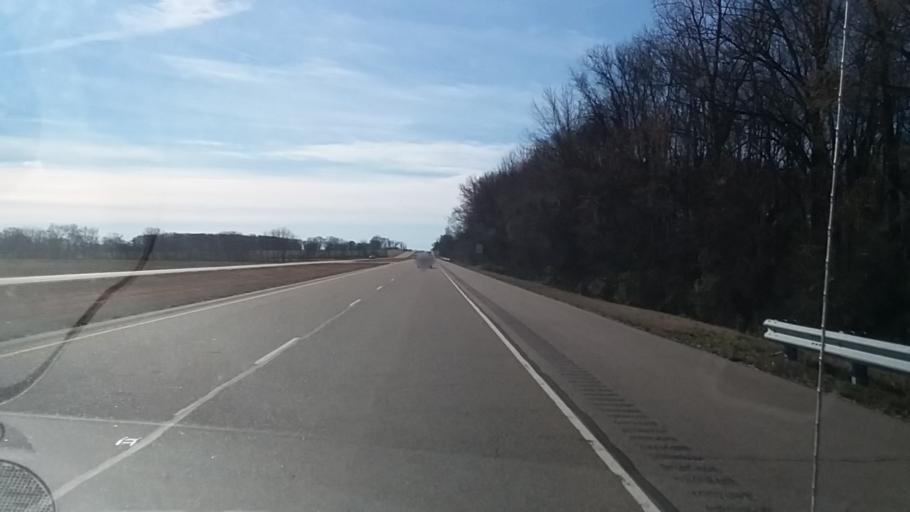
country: US
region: Tennessee
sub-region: Crockett County
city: Alamo
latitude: 35.8797
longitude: -89.2247
